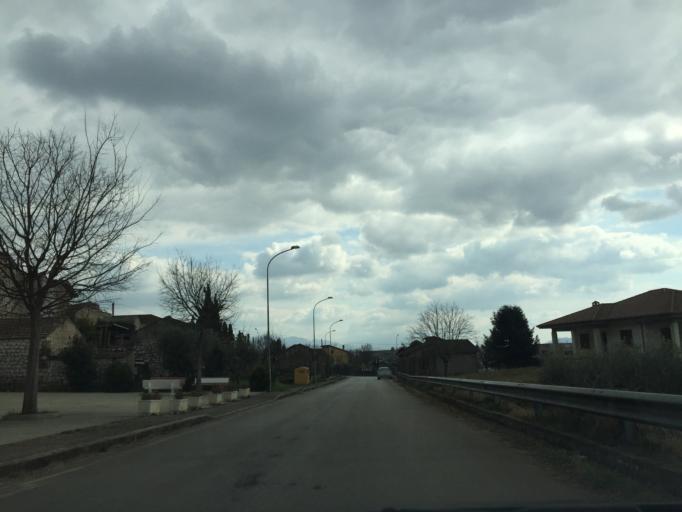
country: IT
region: Latium
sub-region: Provincia di Frosinone
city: Villa Santa Lucia
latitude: 41.4911
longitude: 13.7831
